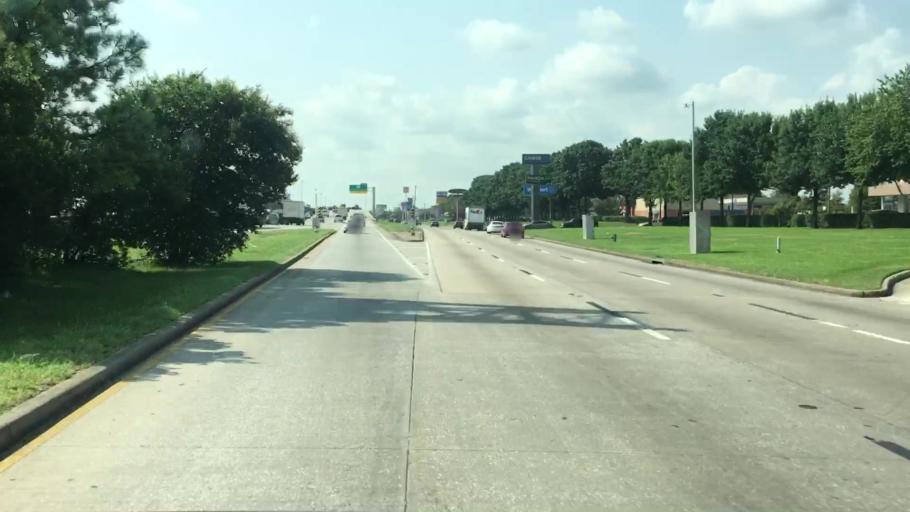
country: US
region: Texas
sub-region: Harris County
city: Aldine
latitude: 29.9194
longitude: -95.4129
